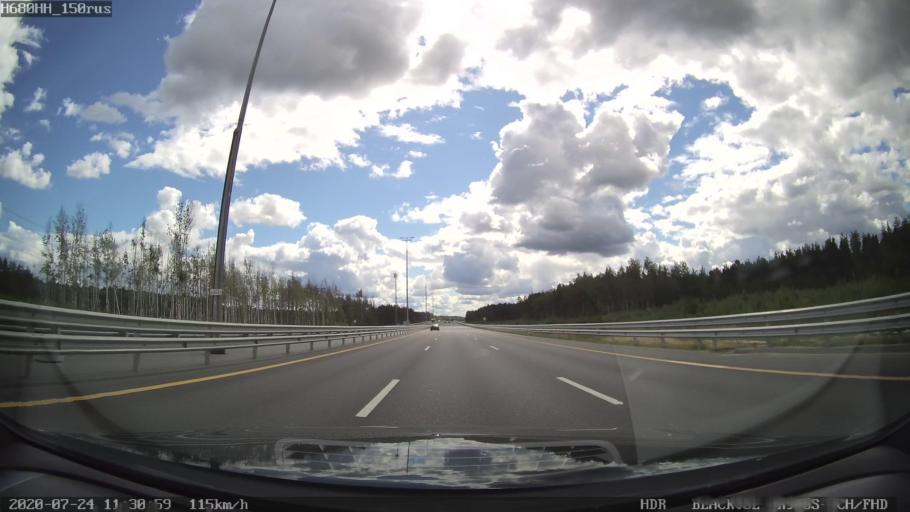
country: RU
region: Leningrad
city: Krasnyy Bor
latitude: 59.6626
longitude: 30.6246
